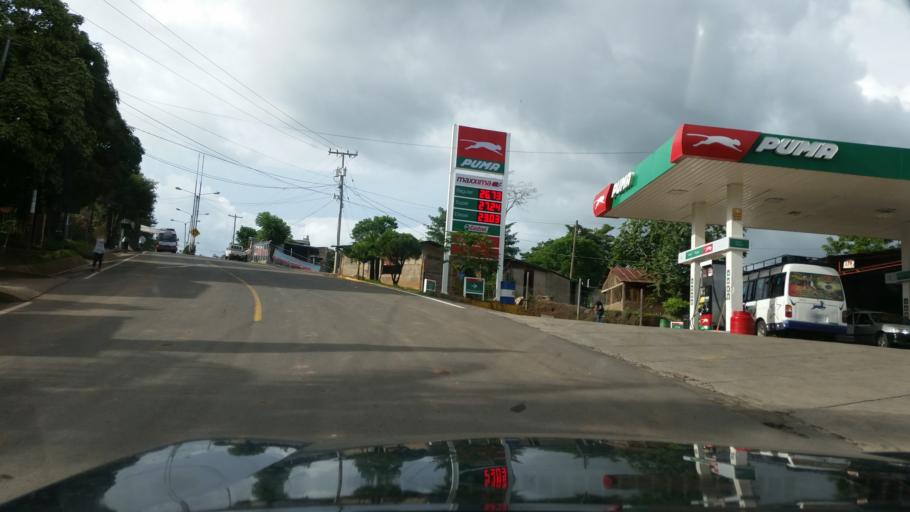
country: NI
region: Matagalpa
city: San Ramon
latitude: 13.1346
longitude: -85.7365
